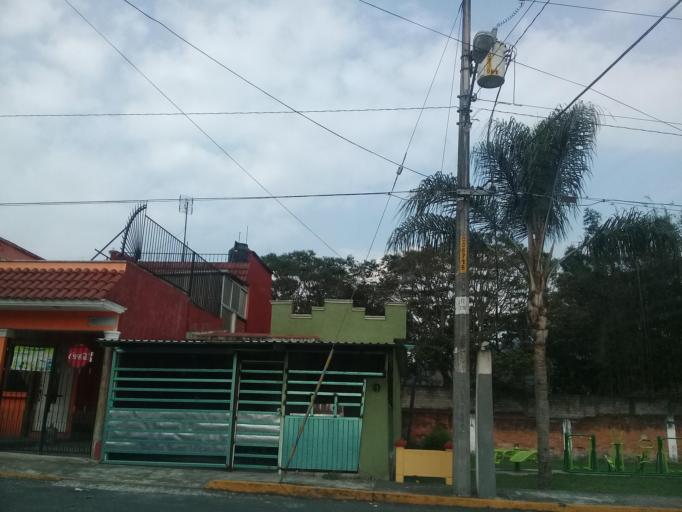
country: MX
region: Veracruz
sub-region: Mariano Escobedo
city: Palmira
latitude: 18.8738
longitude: -97.1079
